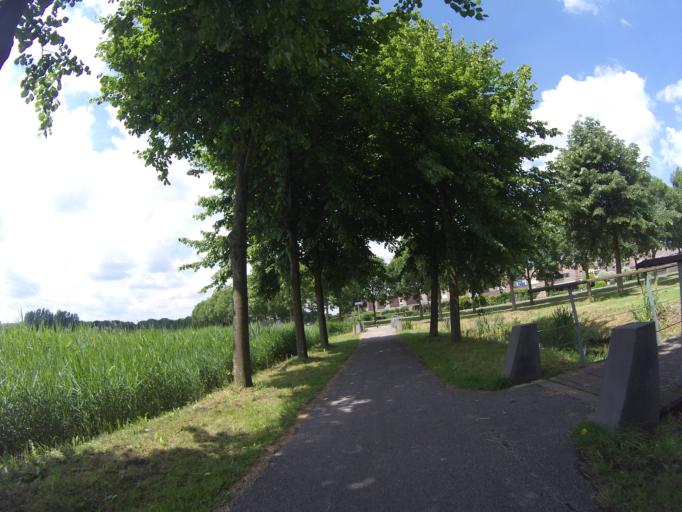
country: NL
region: Utrecht
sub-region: Gemeente Bunschoten
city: Bunschoten
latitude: 52.2430
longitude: 5.3832
